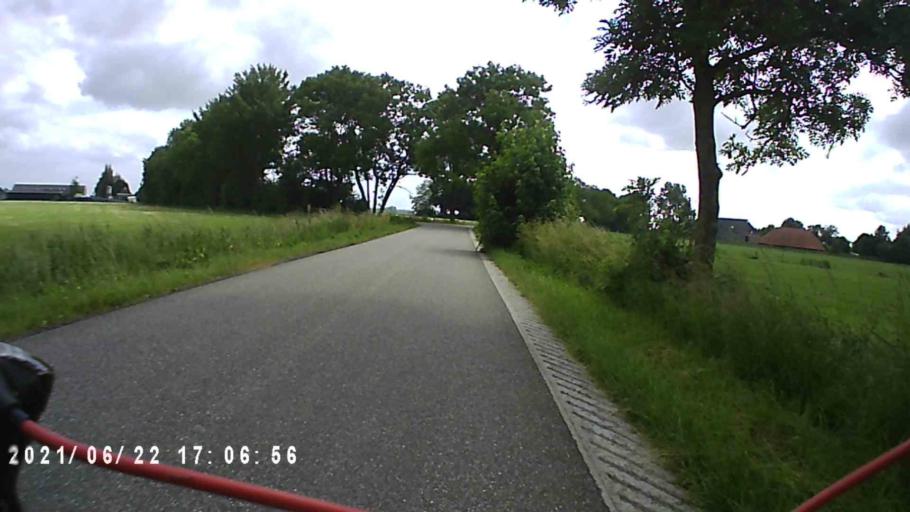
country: NL
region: Groningen
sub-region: Gemeente Bedum
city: Bedum
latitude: 53.2839
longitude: 6.6283
